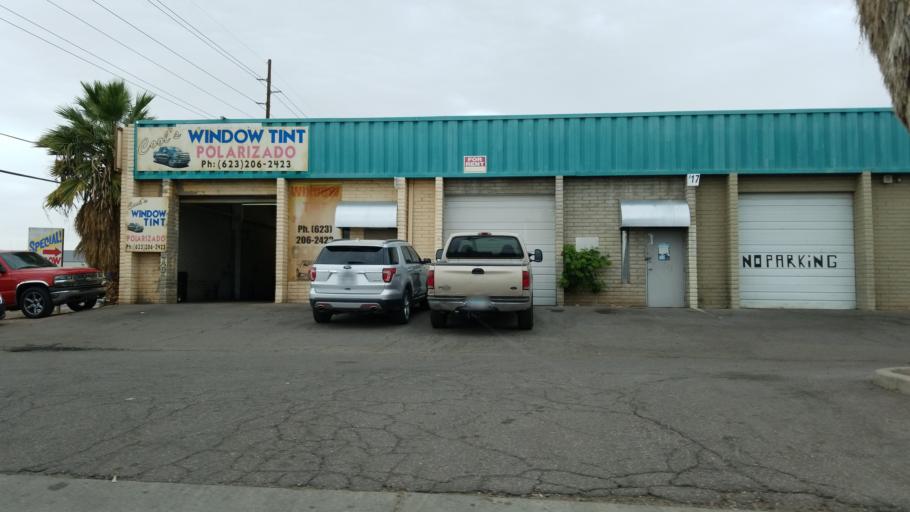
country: US
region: Arizona
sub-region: Maricopa County
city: Phoenix
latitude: 33.4478
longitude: -112.1339
